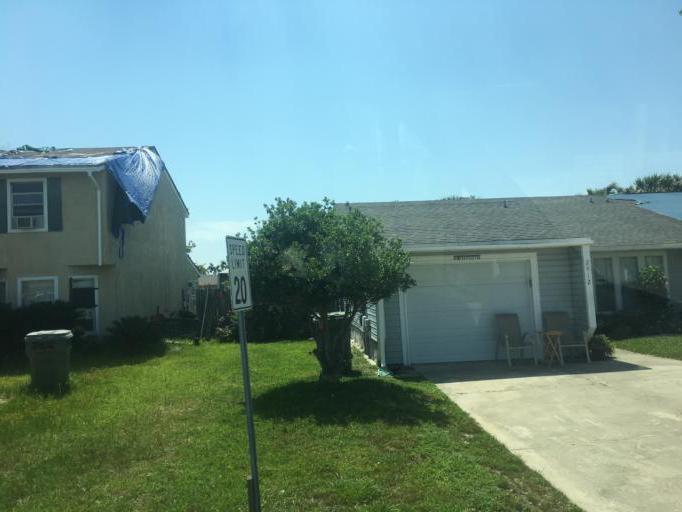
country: US
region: Florida
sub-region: Bay County
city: Lynn Haven
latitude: 30.2214
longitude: -85.6507
